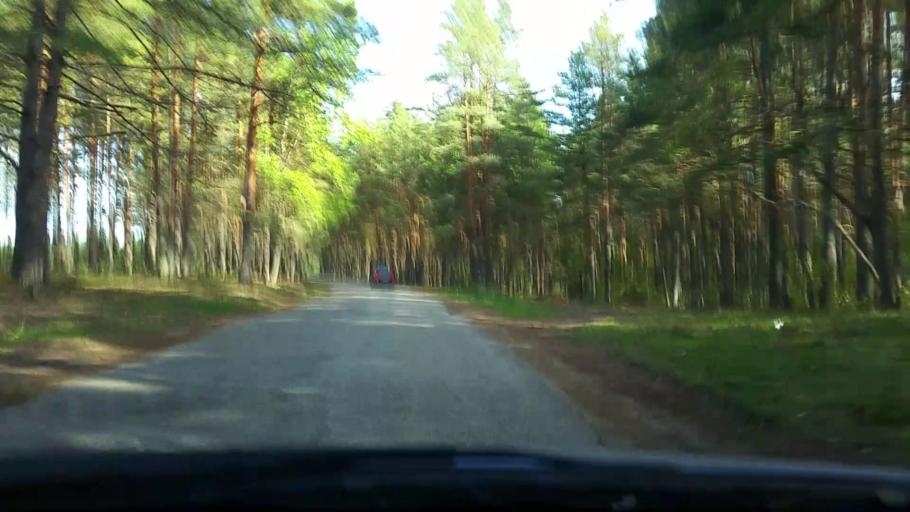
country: LV
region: Adazi
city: Adazi
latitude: 57.1004
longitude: 24.3740
